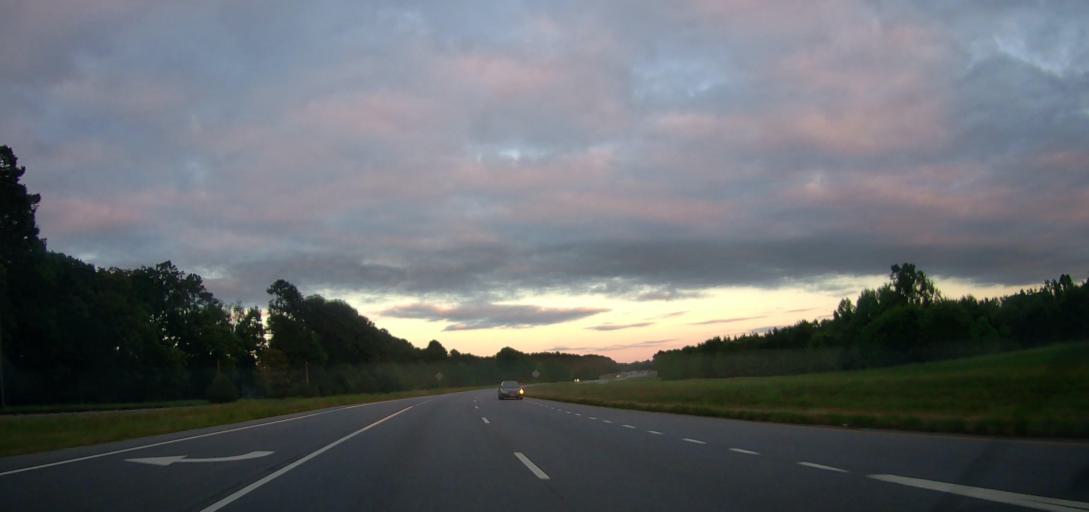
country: US
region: Georgia
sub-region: Clarke County
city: Country Club Estates
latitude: 34.0038
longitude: -83.4501
